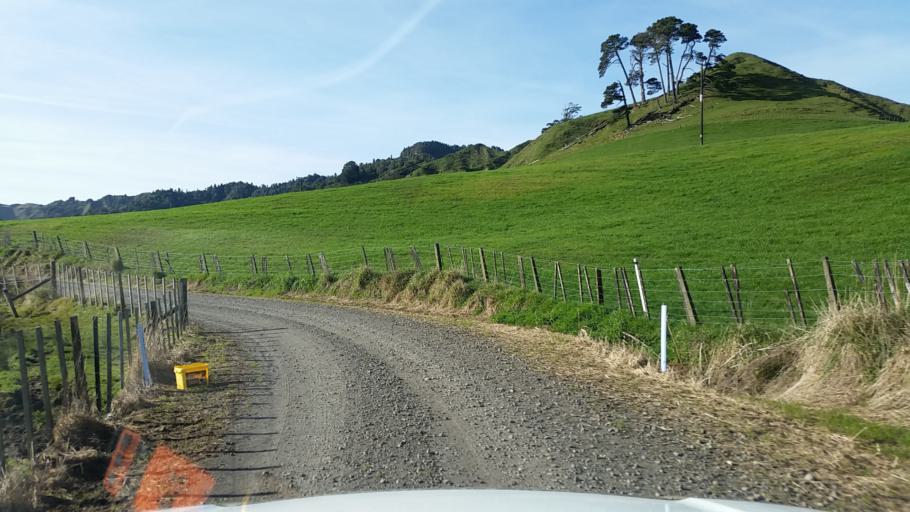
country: NZ
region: Taranaki
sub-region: South Taranaki District
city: Eltham
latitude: -39.3107
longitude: 174.5428
